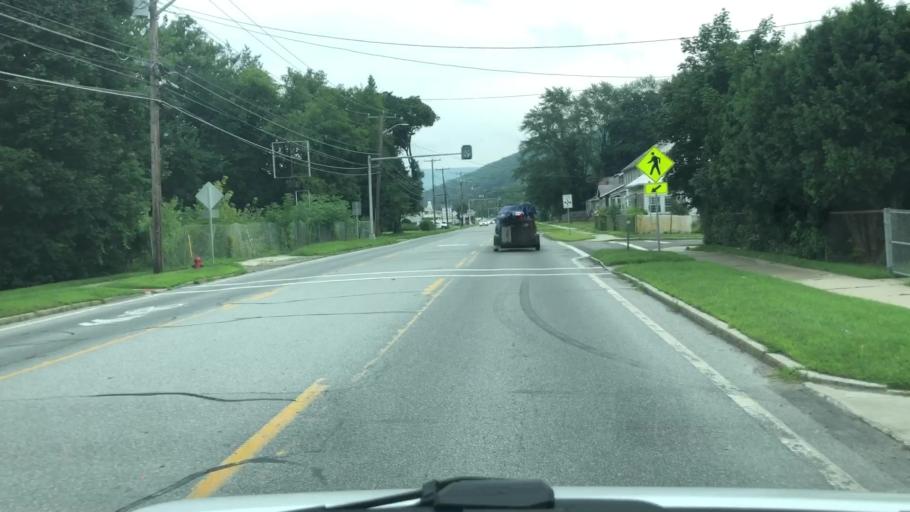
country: US
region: Massachusetts
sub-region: Berkshire County
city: North Adams
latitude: 42.6980
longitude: -73.1457
